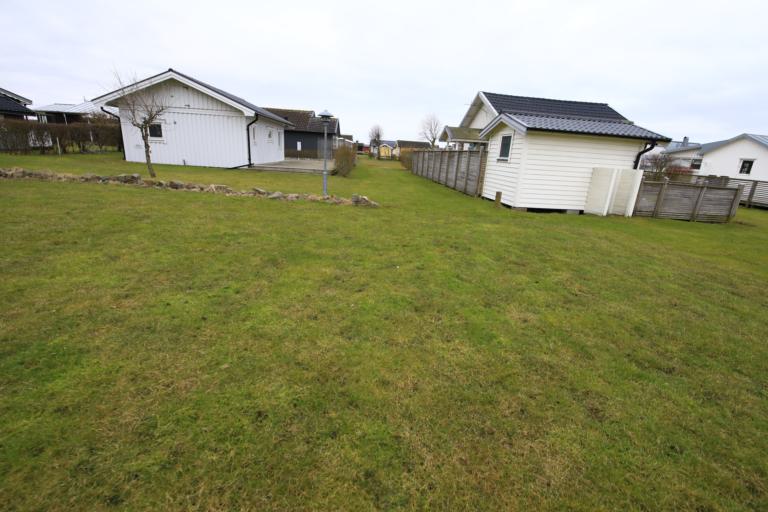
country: SE
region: Halland
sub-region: Varbergs Kommun
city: Traslovslage
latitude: 57.0705
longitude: 12.2771
